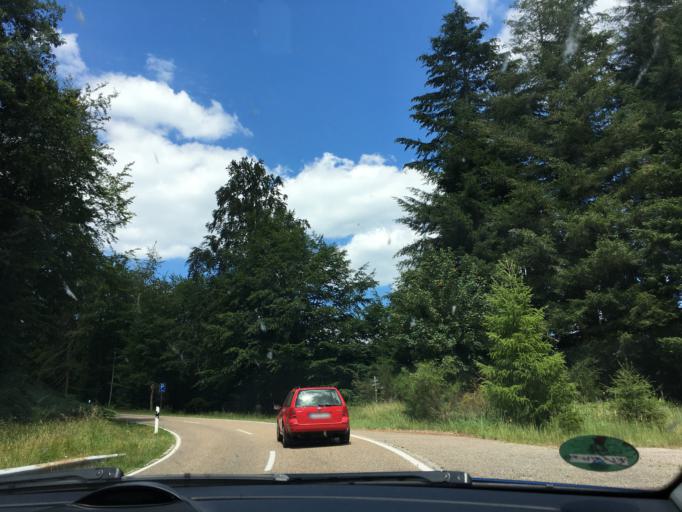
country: DE
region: Rheinland-Pfalz
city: Hauenstein
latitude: 49.2308
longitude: 7.8442
